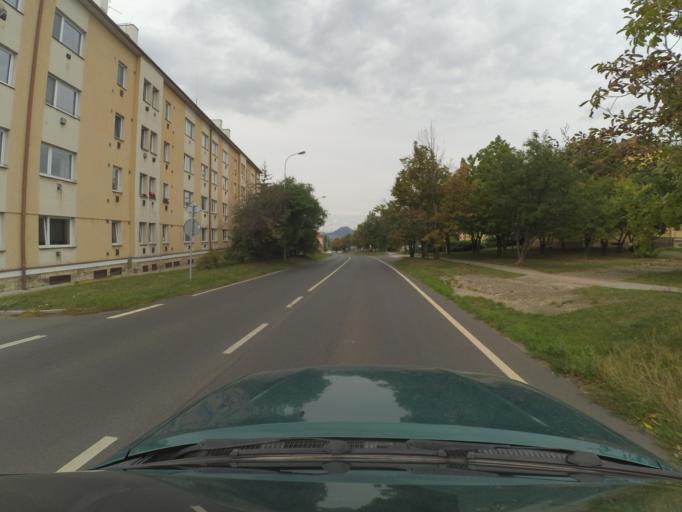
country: CZ
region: Ustecky
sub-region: Okres Louny
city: Louny
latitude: 50.3473
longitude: 13.8058
